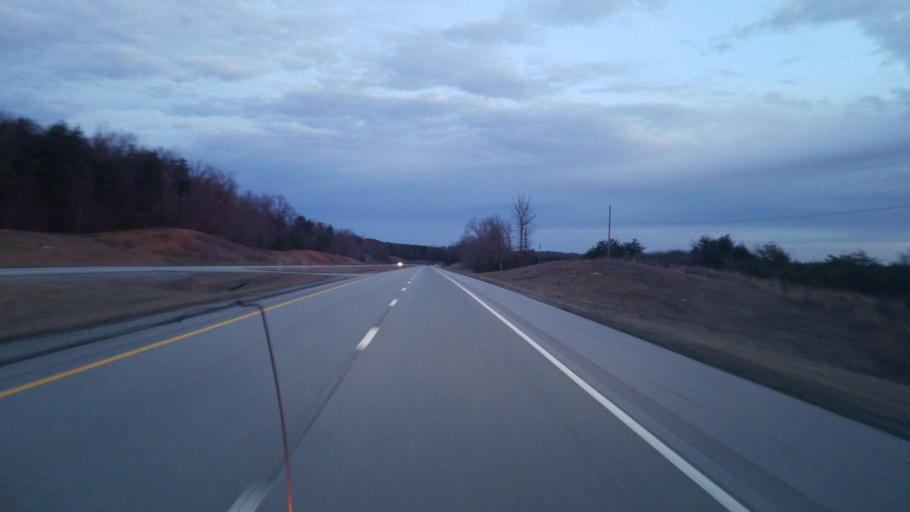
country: US
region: Tennessee
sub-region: Van Buren County
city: Spencer
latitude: 35.6857
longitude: -85.4783
